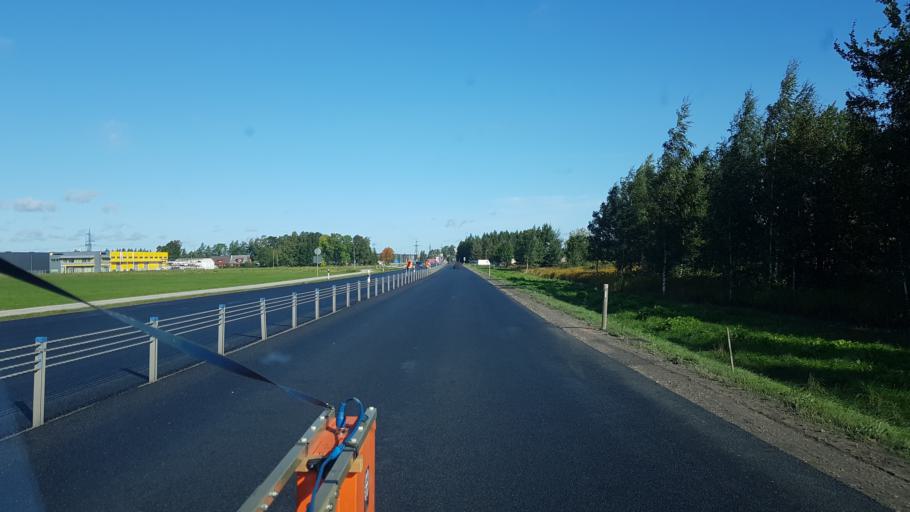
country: EE
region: Tartu
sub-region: Tartu linn
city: Tartu
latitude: 58.3716
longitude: 26.6819
